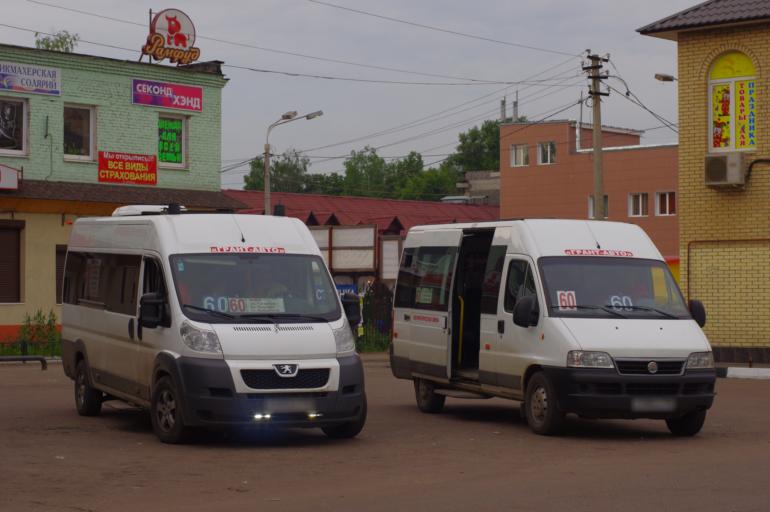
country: RU
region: Moskovskaya
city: Ramenskoye
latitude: 55.5716
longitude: 38.2091
